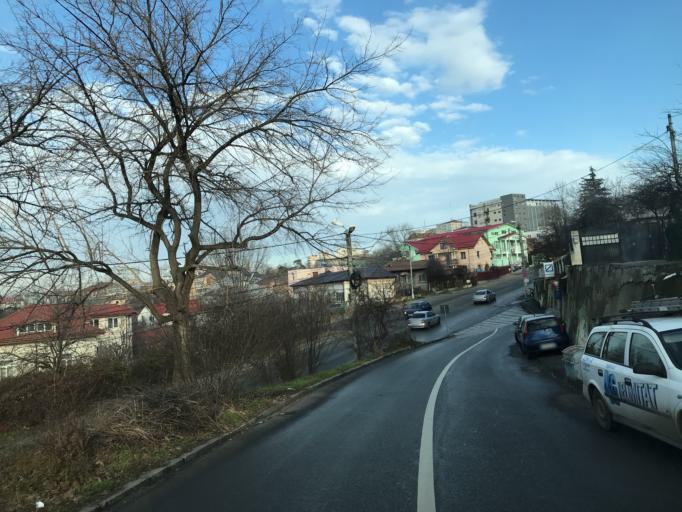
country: RO
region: Olt
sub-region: Municipiul Slatina
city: Slatina
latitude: 44.4275
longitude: 24.3590
